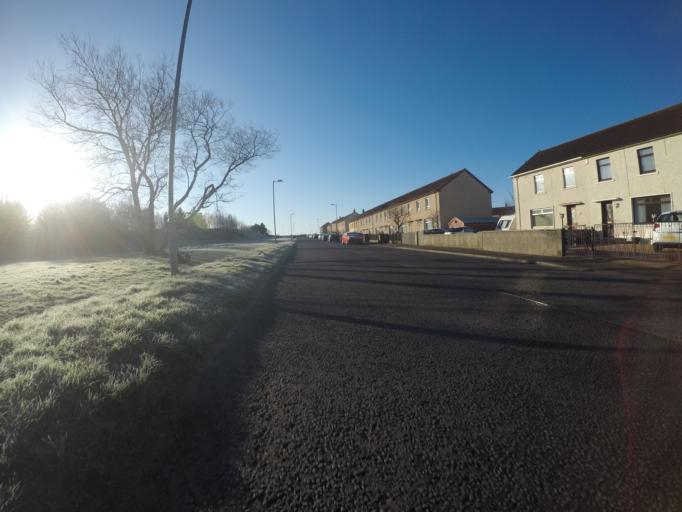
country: GB
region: Scotland
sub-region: North Ayrshire
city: Stevenston
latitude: 55.6315
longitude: -4.7409
